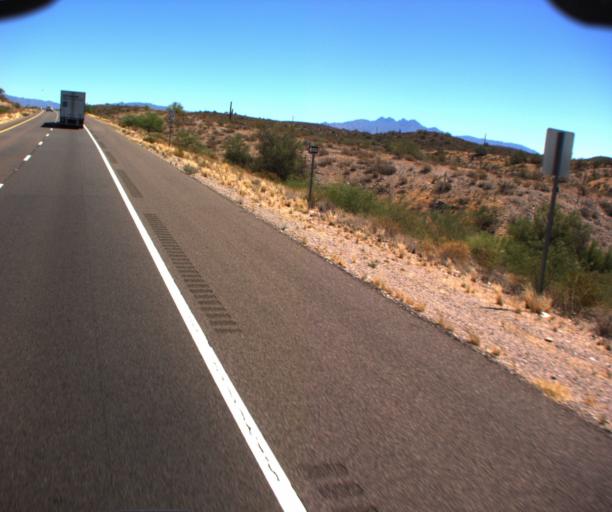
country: US
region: Arizona
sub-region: Maricopa County
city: Fountain Hills
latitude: 33.5939
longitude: -111.5933
